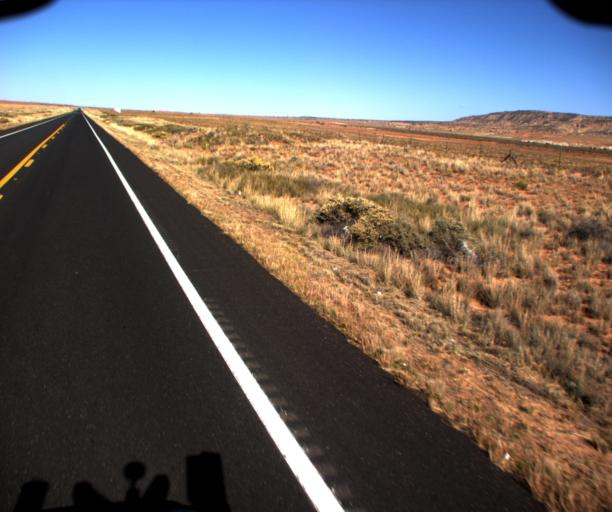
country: US
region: Arizona
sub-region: Coconino County
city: Kaibito
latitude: 36.3591
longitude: -110.9038
